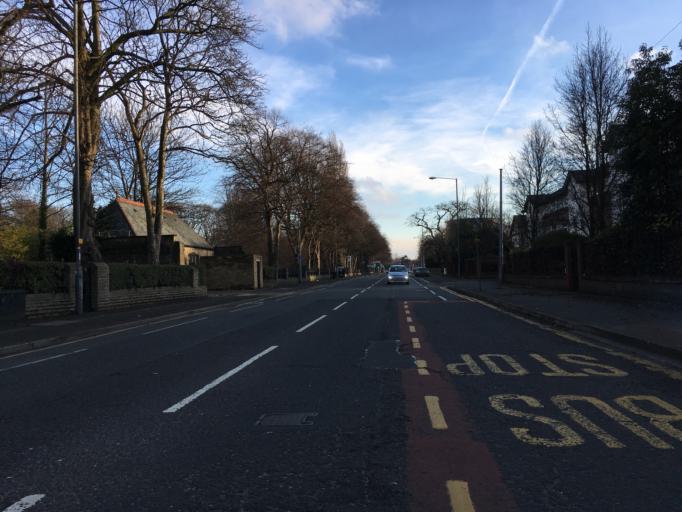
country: GB
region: England
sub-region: Manchester
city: Chorlton cum Hardy
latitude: 53.4276
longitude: -2.2612
